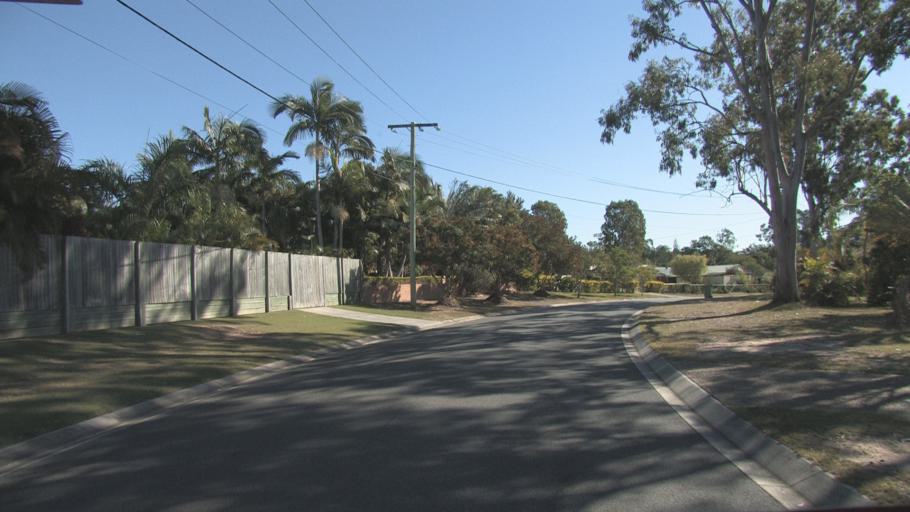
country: AU
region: Queensland
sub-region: Logan
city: Logan Reserve
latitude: -27.6842
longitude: 153.0640
